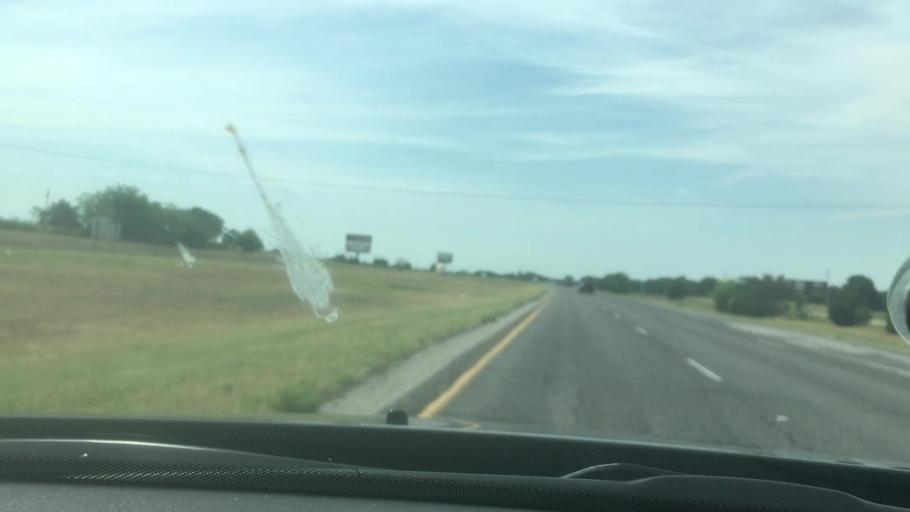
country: US
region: Oklahoma
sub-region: Garvin County
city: Wynnewood
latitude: 34.5677
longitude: -97.1974
